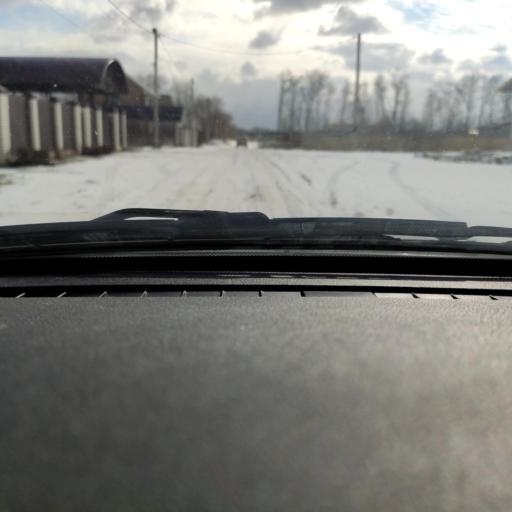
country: RU
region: Voronezj
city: Novaya Usman'
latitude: 51.6600
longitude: 39.4631
